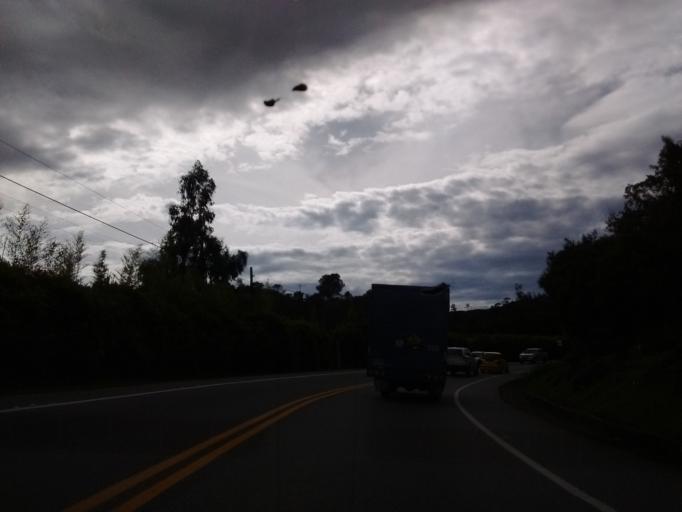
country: CO
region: Antioquia
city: Santuario
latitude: 6.1003
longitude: -75.2266
